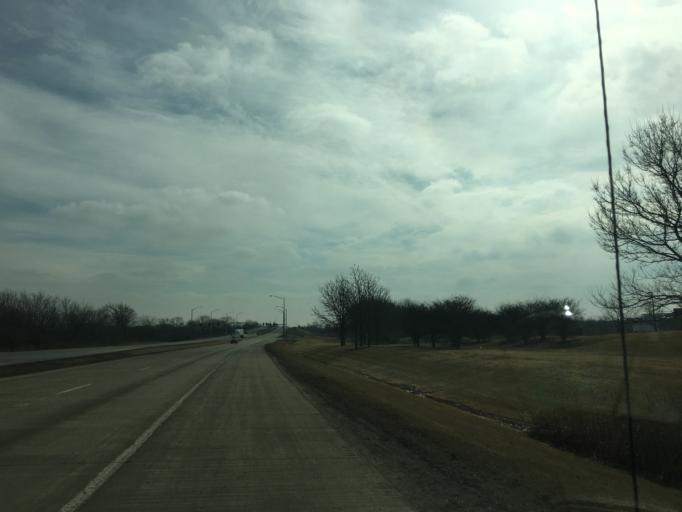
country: US
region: Illinois
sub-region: Cook County
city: Streamwood
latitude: 42.0796
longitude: -88.2088
